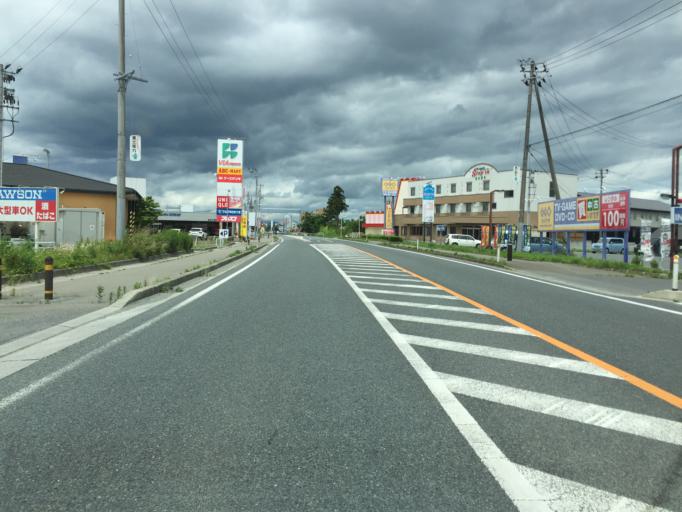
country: JP
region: Fukushima
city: Namie
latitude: 37.6280
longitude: 140.9898
